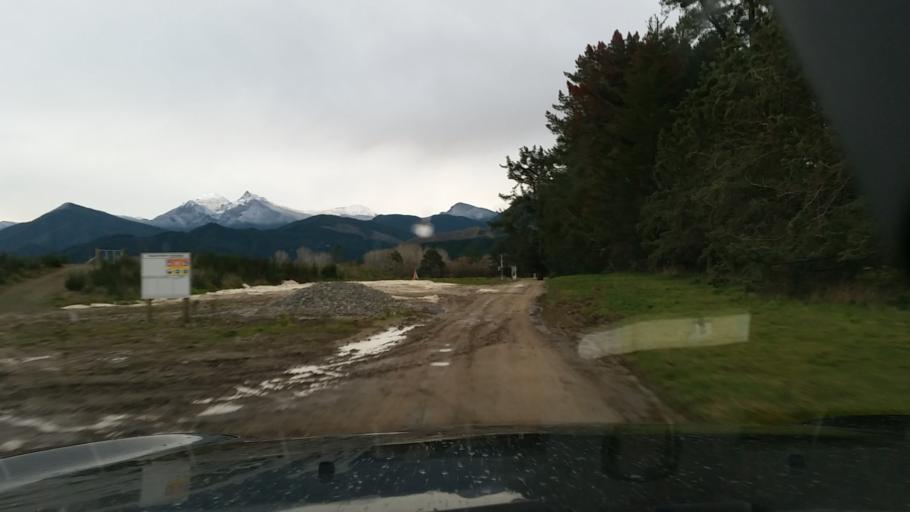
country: NZ
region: Nelson
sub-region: Nelson City
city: Nelson
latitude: -41.5614
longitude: 173.5217
